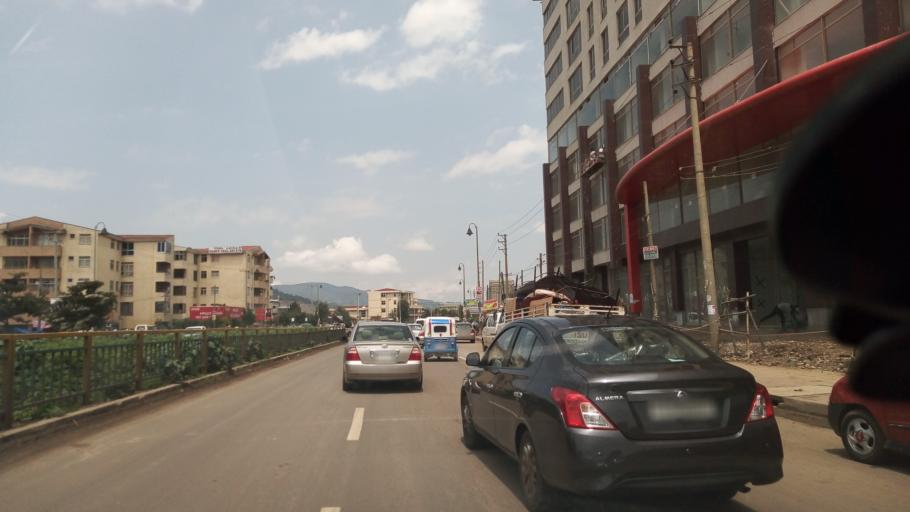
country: ET
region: Adis Abeba
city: Addis Ababa
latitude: 8.9646
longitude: 38.7193
